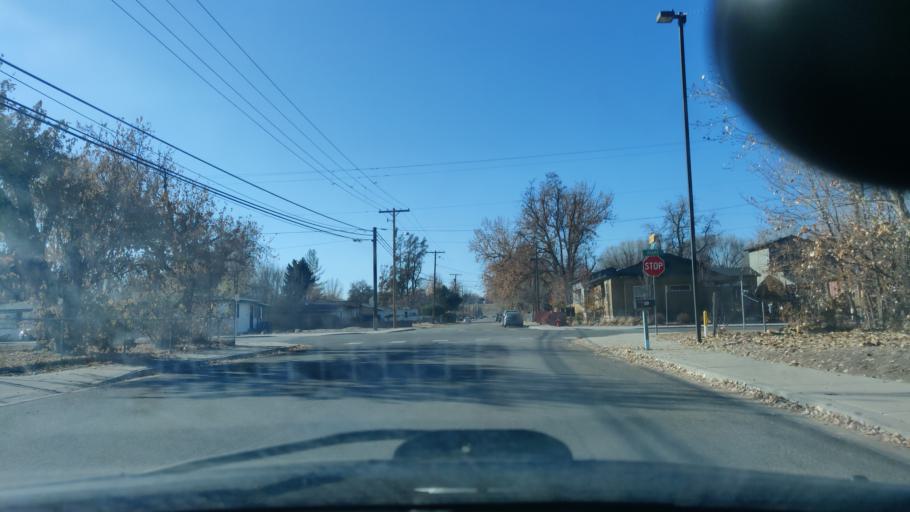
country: US
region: Idaho
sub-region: Ada County
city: Garden City
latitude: 43.6360
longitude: -116.2485
